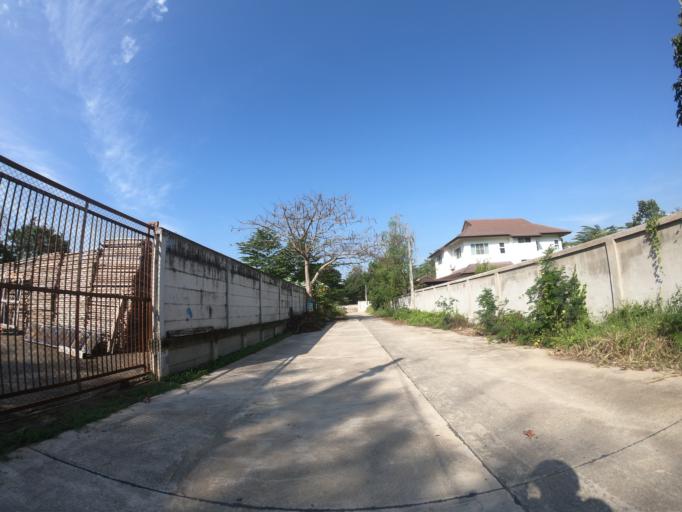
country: TH
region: Chiang Mai
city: Chiang Mai
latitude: 18.7508
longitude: 98.9841
